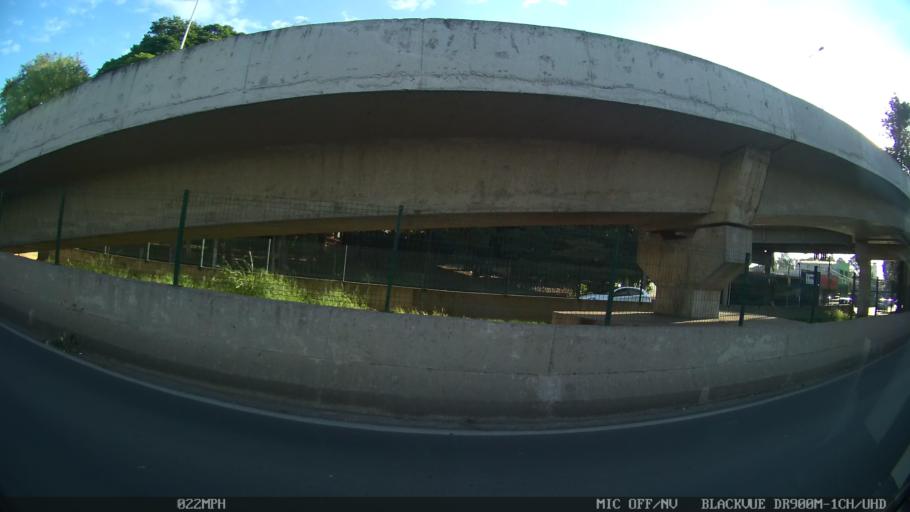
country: BR
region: Sao Paulo
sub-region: Piracicaba
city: Piracicaba
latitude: -22.7160
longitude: -47.6463
